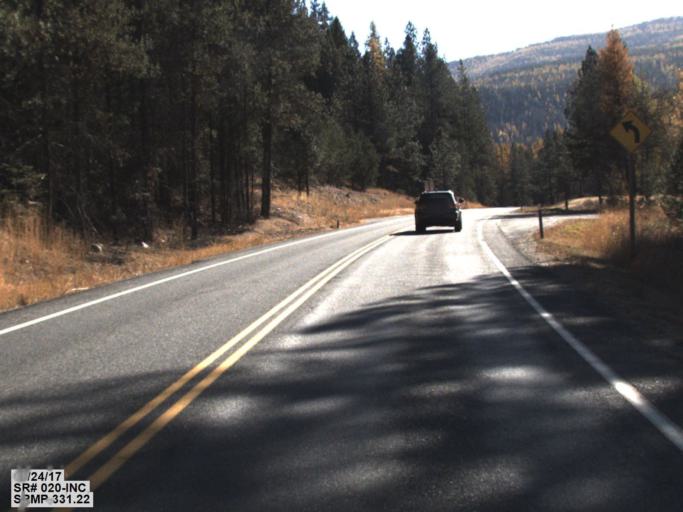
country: US
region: Washington
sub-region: Stevens County
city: Kettle Falls
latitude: 48.5863
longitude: -118.3047
